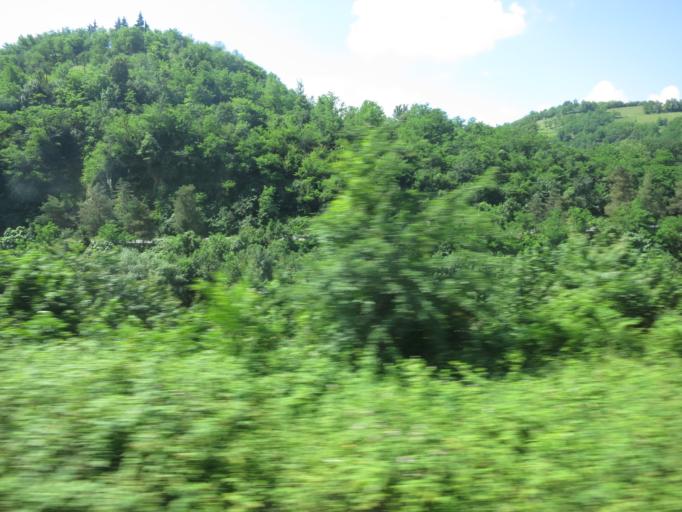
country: GE
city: Shorapani
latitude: 42.0937
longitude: 43.0977
